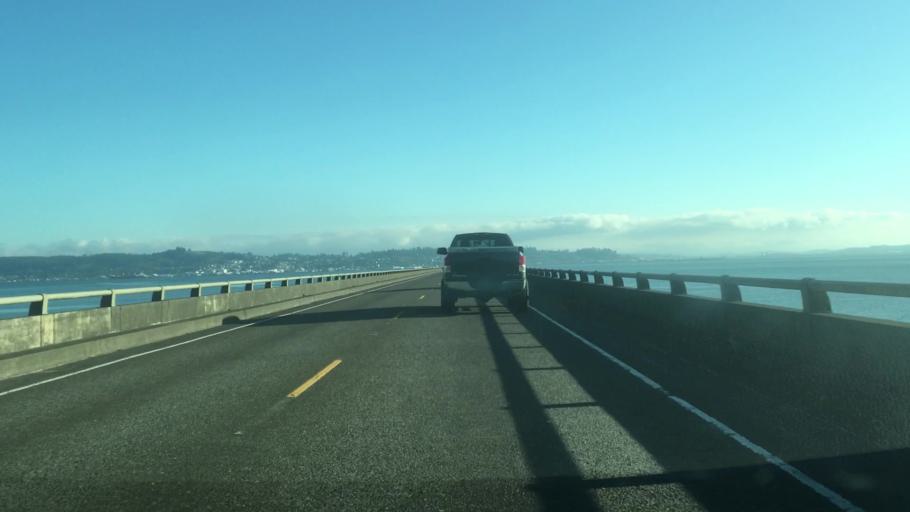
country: US
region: Oregon
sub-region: Clatsop County
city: Astoria
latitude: 46.2312
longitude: -123.8701
